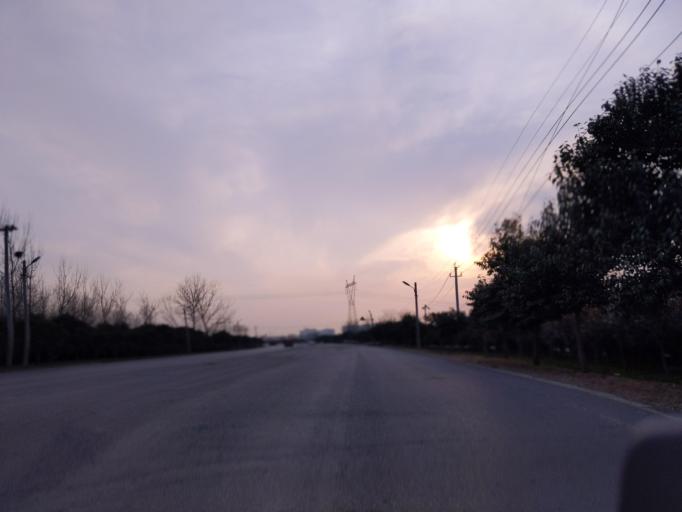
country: CN
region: Henan Sheng
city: Puyang
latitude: 35.8188
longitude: 114.9723
